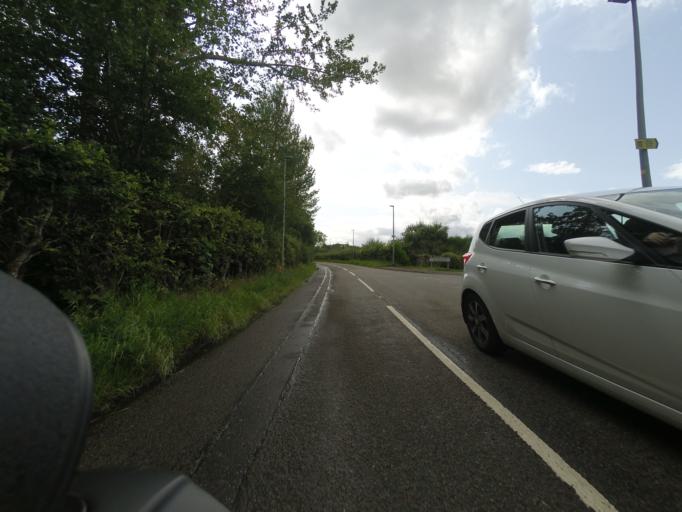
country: GB
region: Scotland
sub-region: Highland
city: Tain
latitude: 57.7414
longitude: -4.0784
